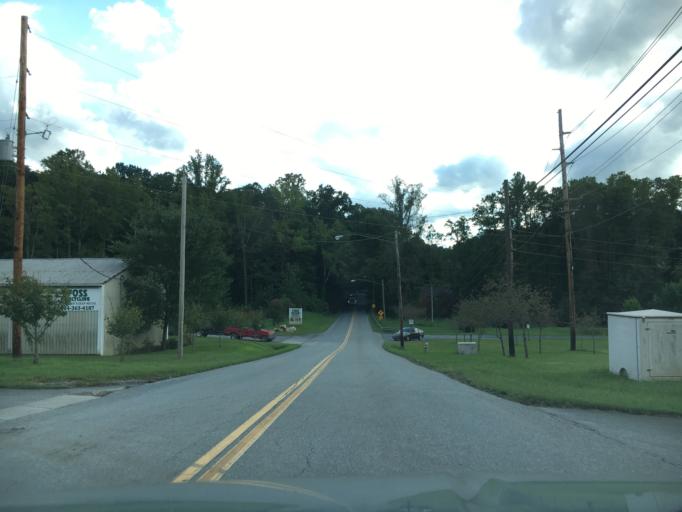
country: US
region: Virginia
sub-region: City of Lynchburg
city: Lynchburg
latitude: 37.3789
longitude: -79.1452
